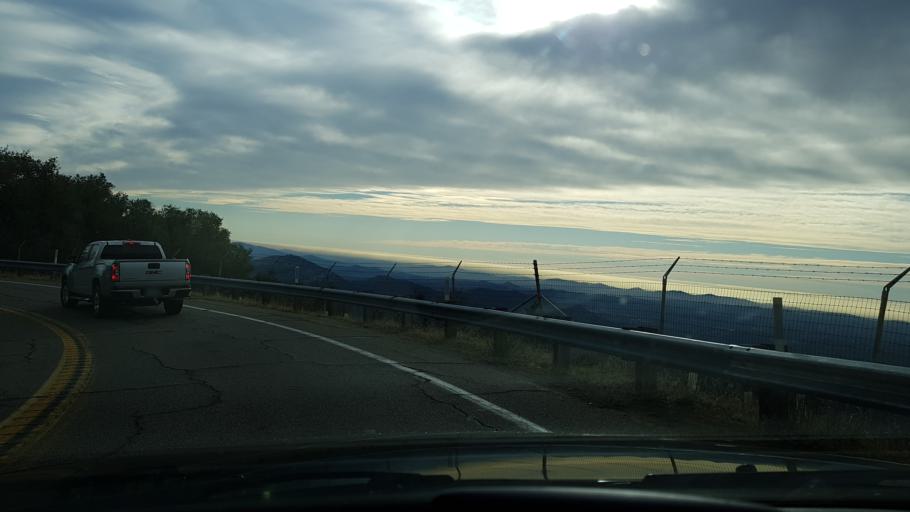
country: US
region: California
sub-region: Riverside County
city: Aguanga
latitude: 33.3056
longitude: -116.8727
